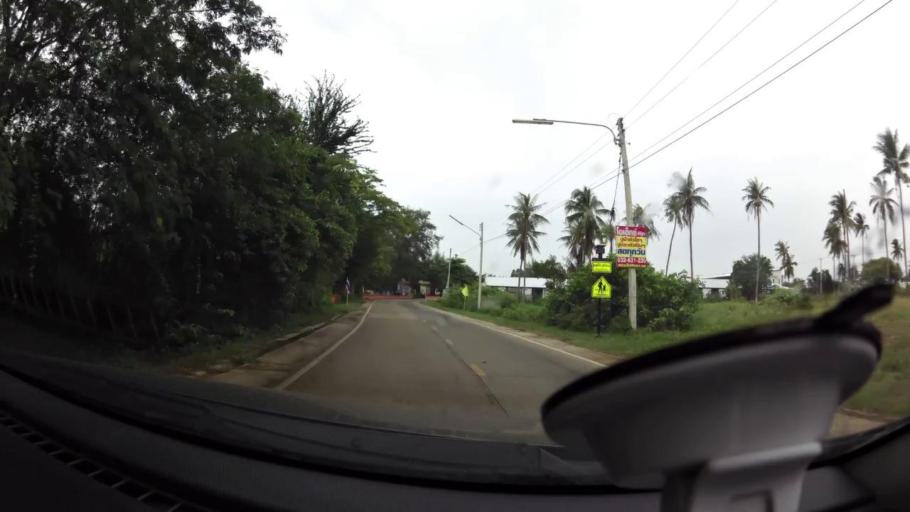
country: TH
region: Prachuap Khiri Khan
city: Pran Buri
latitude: 12.3911
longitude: 99.9824
